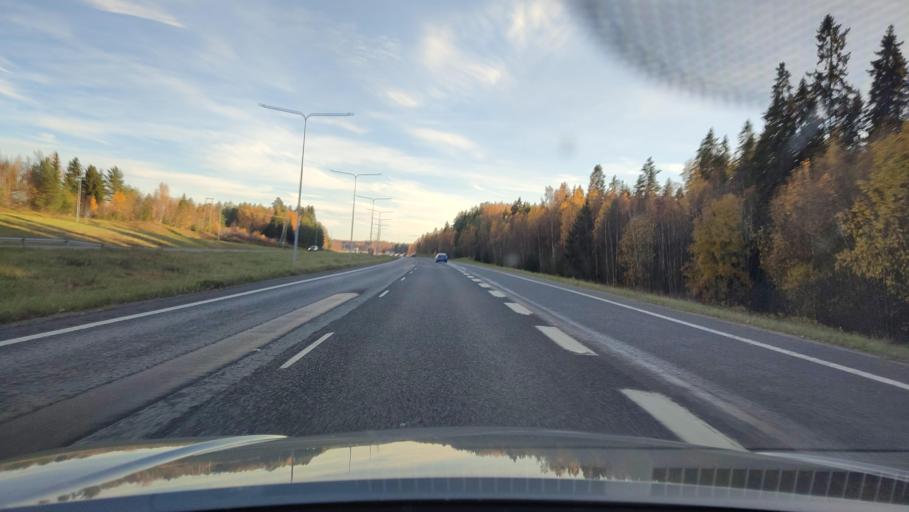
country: FI
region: Ostrobothnia
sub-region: Vaasa
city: Ristinummi
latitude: 63.0535
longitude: 21.7142
